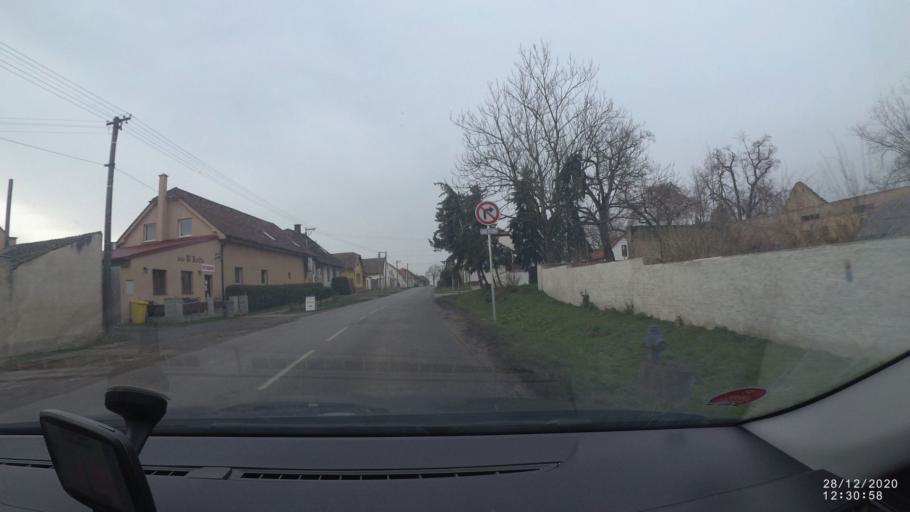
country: CZ
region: Central Bohemia
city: Kostelec nad Labem
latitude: 50.2008
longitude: 14.5933
